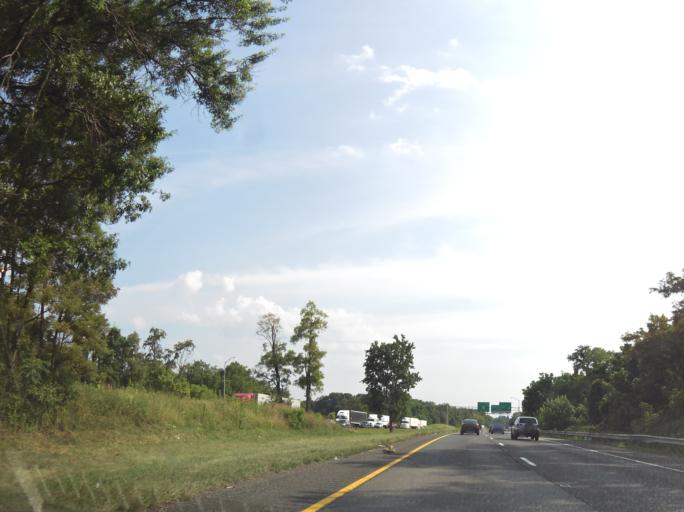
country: US
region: Maryland
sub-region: Washington County
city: Fountainhead-Orchard Hills
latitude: 39.6706
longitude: -77.7356
